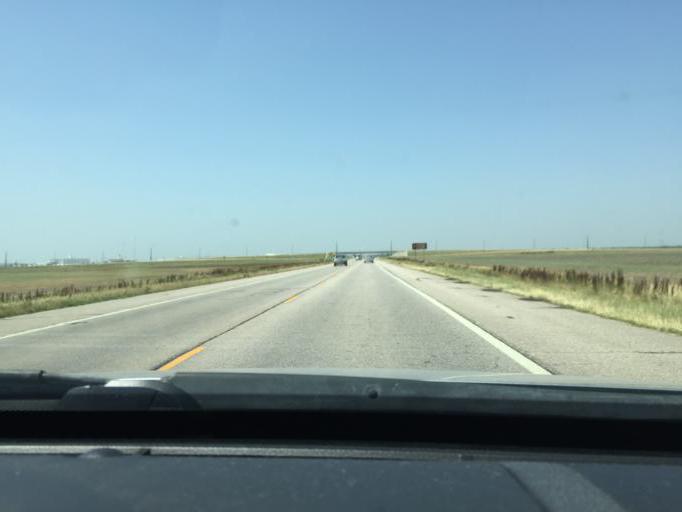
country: US
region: Kansas
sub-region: Reno County
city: South Hutchinson
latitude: 38.0216
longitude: -97.8668
